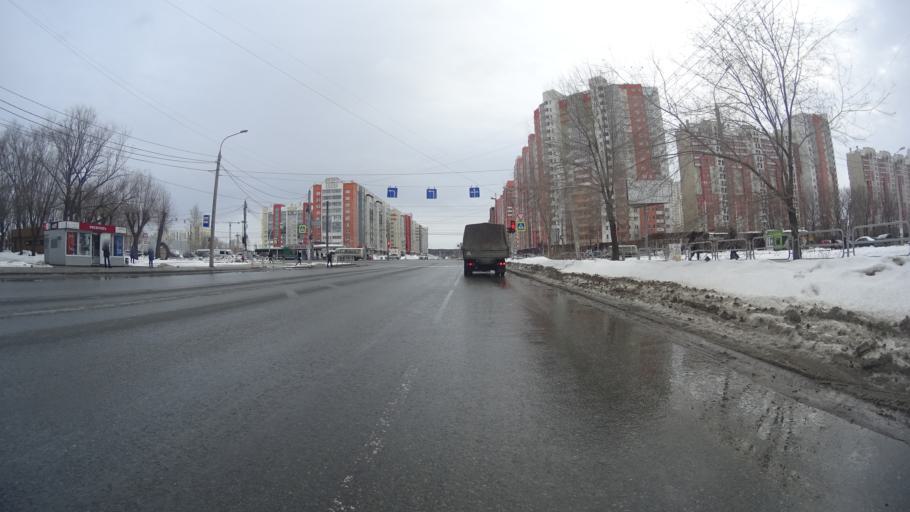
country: RU
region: Chelyabinsk
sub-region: Gorod Chelyabinsk
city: Chelyabinsk
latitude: 55.1772
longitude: 61.3108
